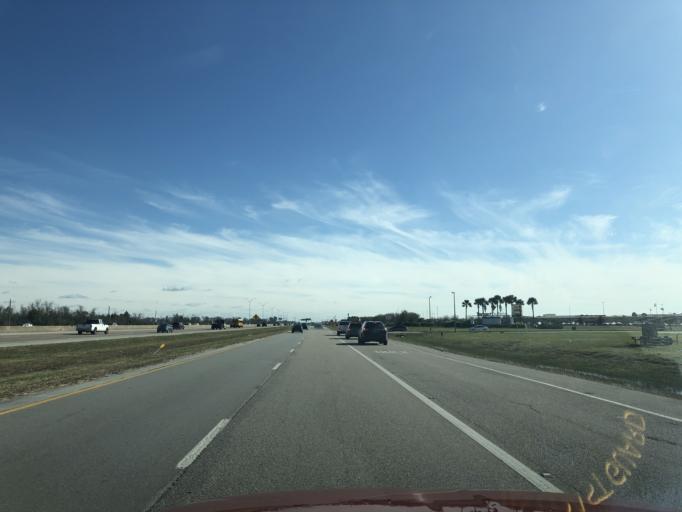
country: US
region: Texas
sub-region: Galveston County
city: Dickinson
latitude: 29.4289
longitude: -95.0595
